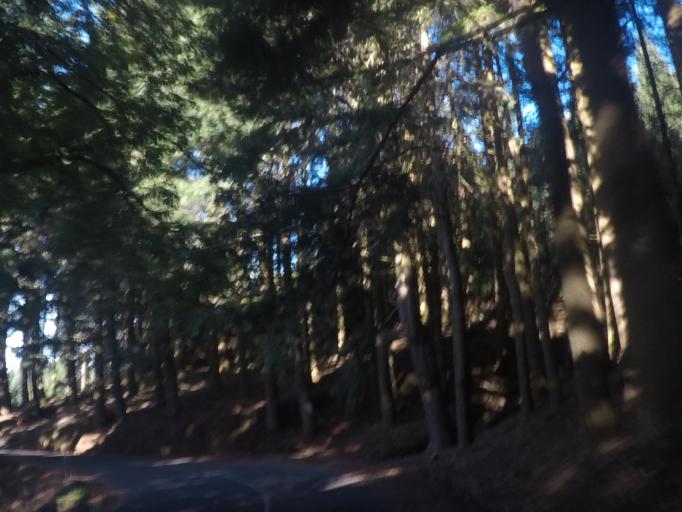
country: PT
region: Madeira
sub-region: Funchal
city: Nossa Senhora do Monte
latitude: 32.7092
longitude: -16.8909
